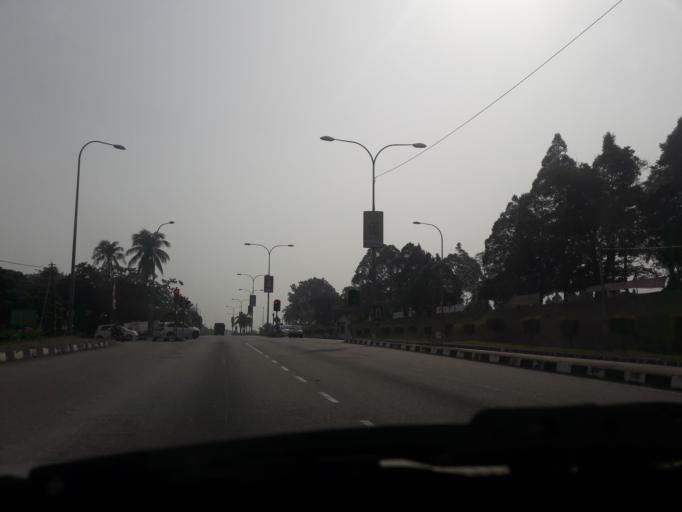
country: MY
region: Kedah
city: Kulim
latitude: 5.3590
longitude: 100.5441
